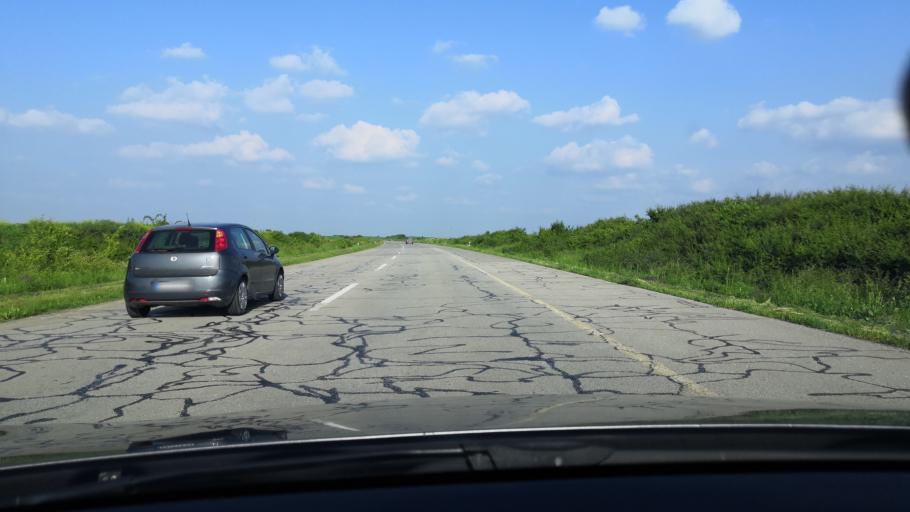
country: RS
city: Beska
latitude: 45.0907
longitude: 20.0454
